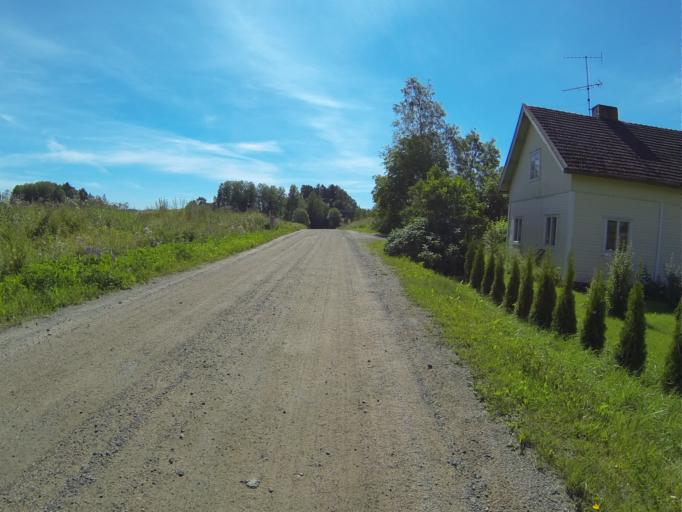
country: FI
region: Varsinais-Suomi
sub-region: Salo
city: Salo
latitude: 60.3070
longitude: 23.1077
